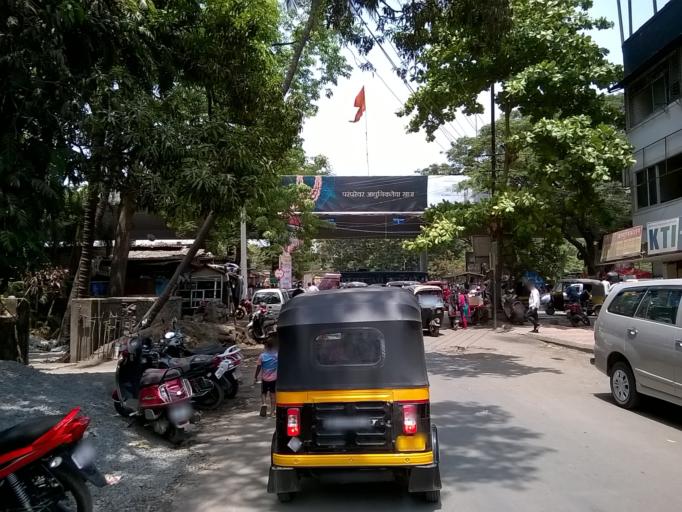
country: IN
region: Maharashtra
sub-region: Raigarh
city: Panvel
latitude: 18.9878
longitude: 73.1153
